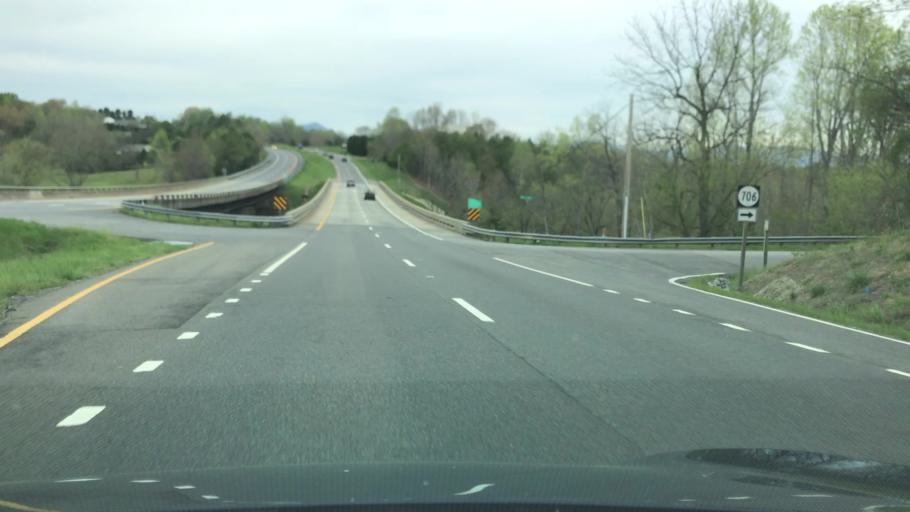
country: US
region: Virginia
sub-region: Bedford County
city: Forest
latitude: 37.3079
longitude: -79.3929
